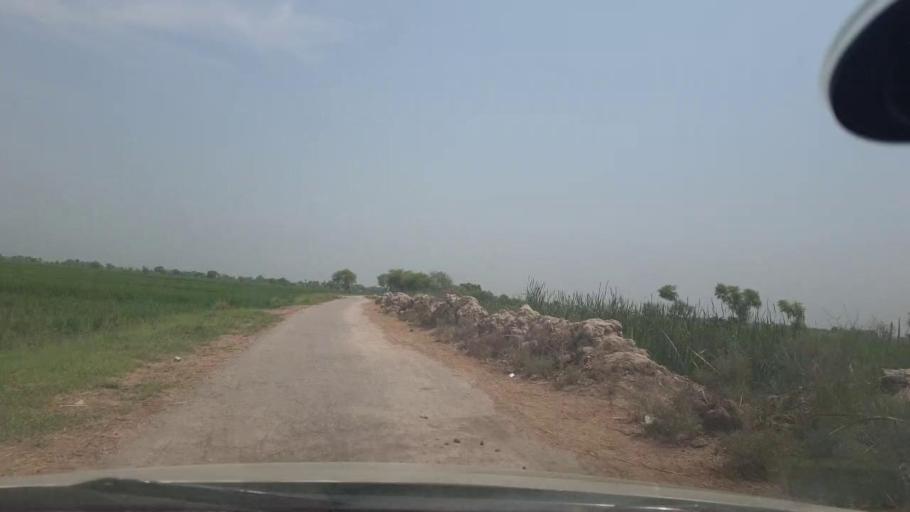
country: PK
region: Sindh
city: Jacobabad
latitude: 28.1798
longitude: 68.3798
